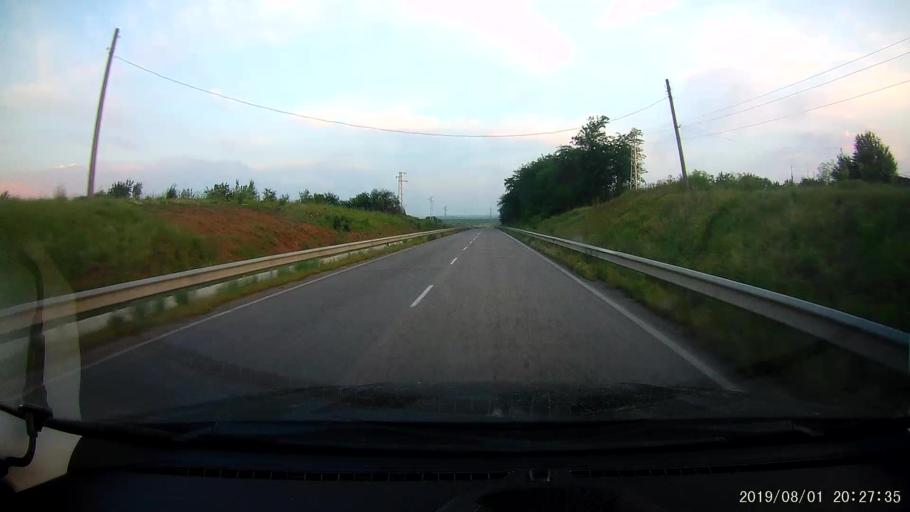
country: BG
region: Yambol
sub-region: Obshtina Elkhovo
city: Elkhovo
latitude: 42.1775
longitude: 26.5842
